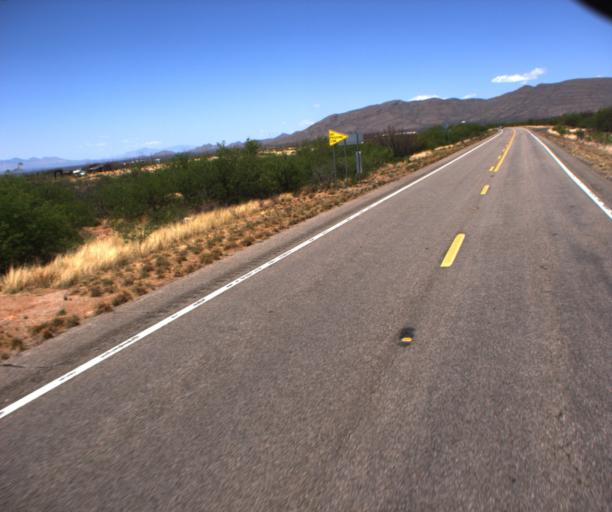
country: US
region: Arizona
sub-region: Cochise County
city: Bisbee
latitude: 31.5420
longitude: -110.0103
